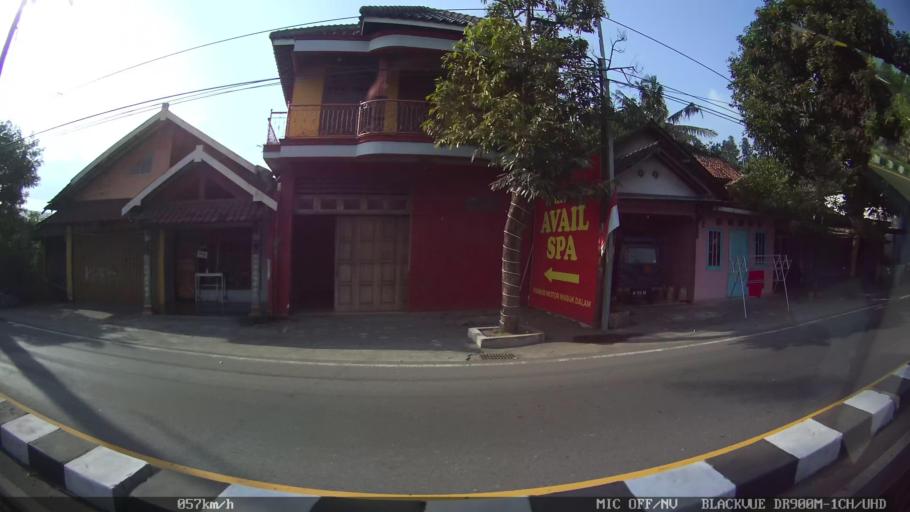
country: ID
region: Daerah Istimewa Yogyakarta
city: Kasihan
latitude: -7.8217
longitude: 110.3259
